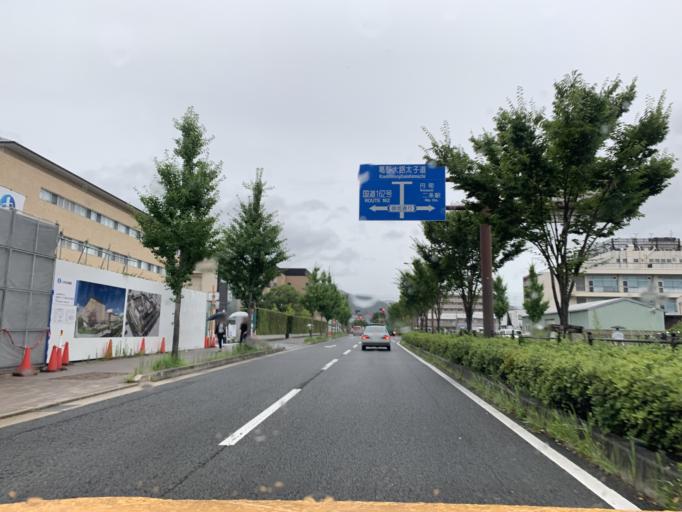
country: JP
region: Kyoto
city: Kyoto
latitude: 35.0095
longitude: 135.7195
